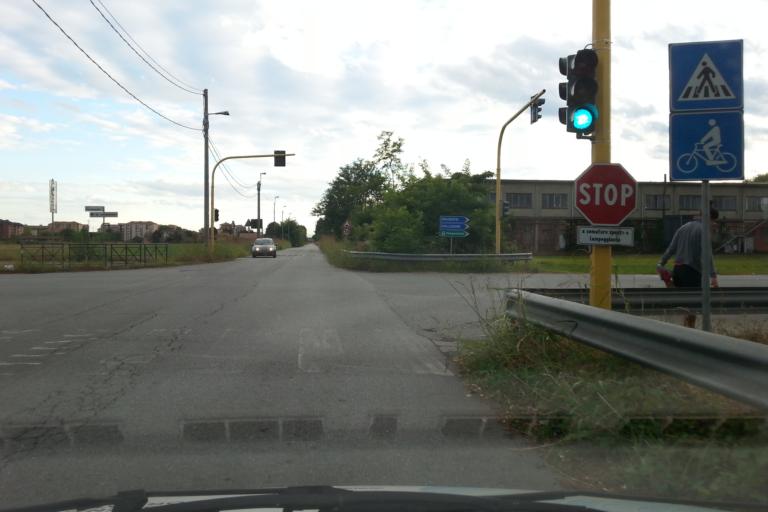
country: IT
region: Piedmont
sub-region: Provincia di Torino
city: Savonera
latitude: 45.1224
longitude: 7.6179
